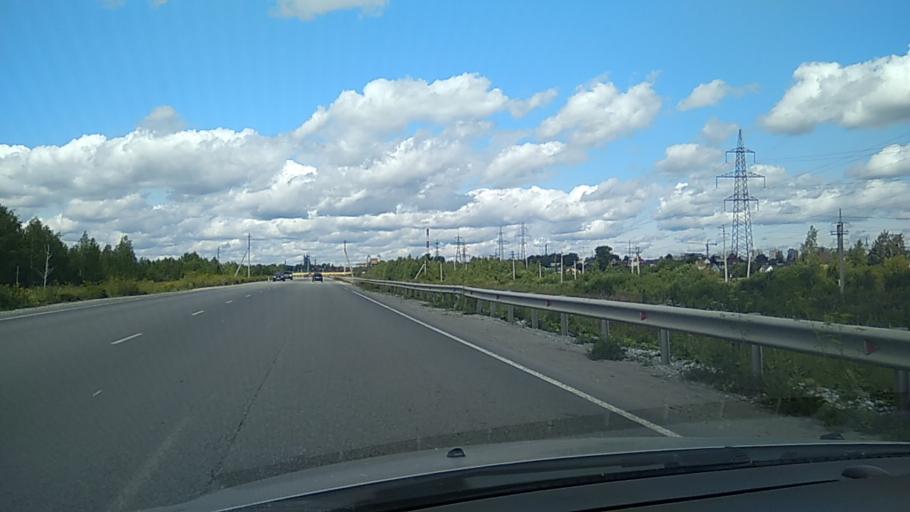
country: RU
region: Sverdlovsk
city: Verkhnyaya Pyshma
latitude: 56.9486
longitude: 60.5965
